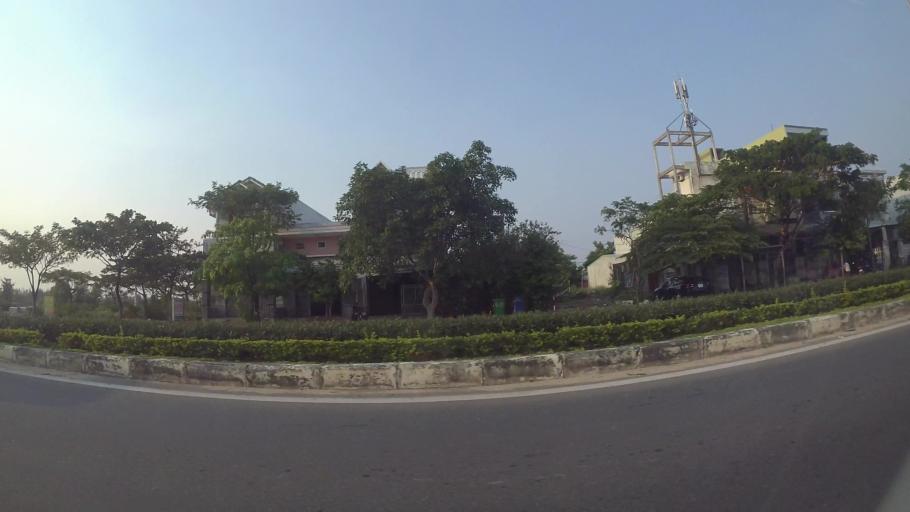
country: VN
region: Da Nang
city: Ngu Hanh Son
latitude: 15.9831
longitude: 108.2524
